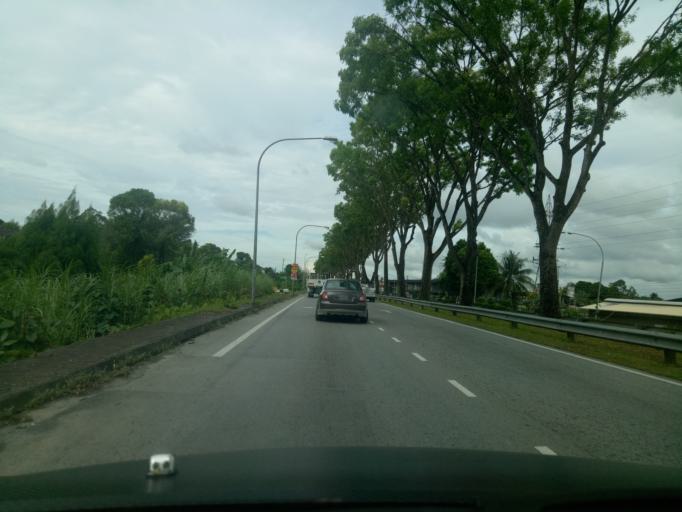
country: MY
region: Sarawak
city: Kuching
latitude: 1.5454
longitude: 110.3777
